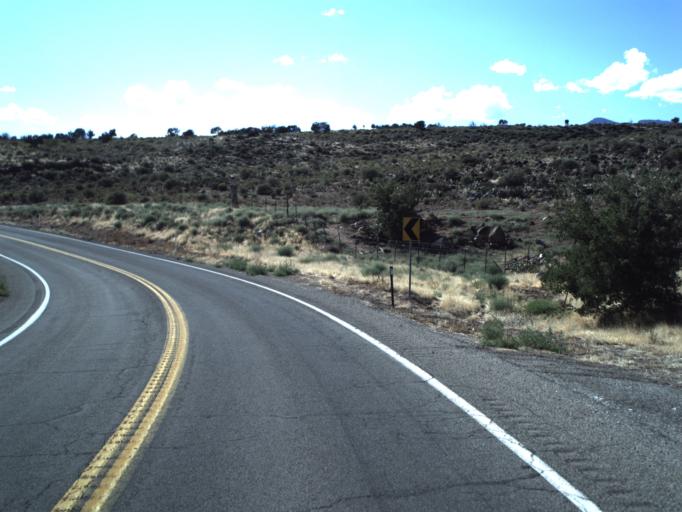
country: US
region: Utah
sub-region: Washington County
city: Toquerville
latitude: 37.2607
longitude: -113.2881
